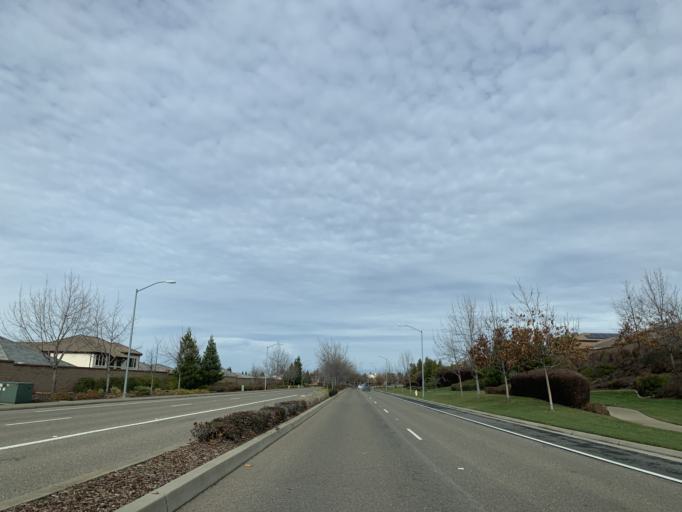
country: US
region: California
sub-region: El Dorado County
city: El Dorado Hills
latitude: 38.6676
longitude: -121.0975
